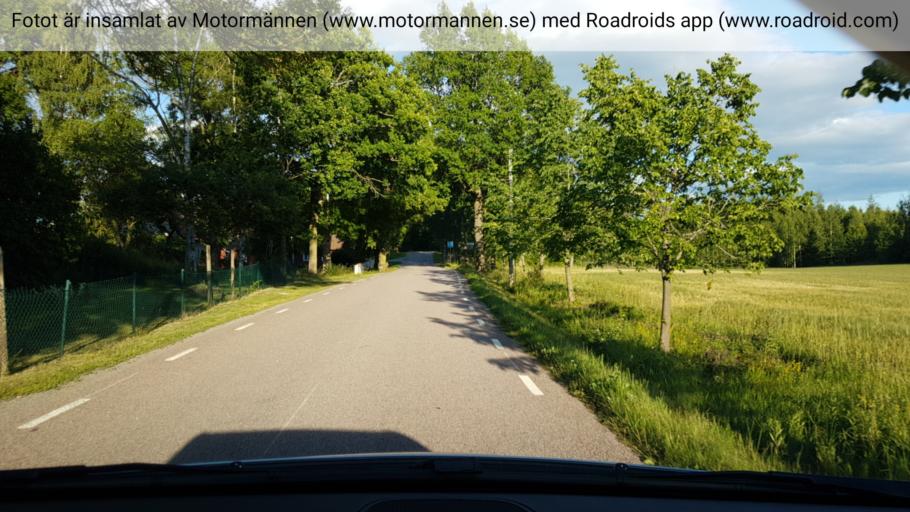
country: SE
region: Vaestmanland
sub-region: Vasteras
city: Tillberga
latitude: 59.6948
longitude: 16.6594
